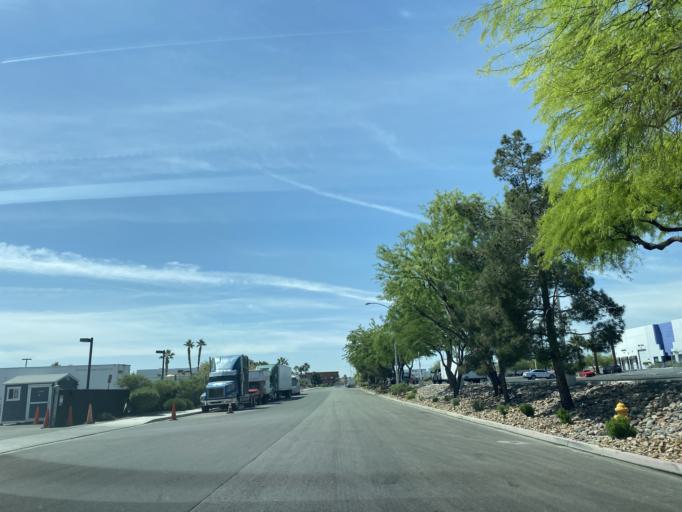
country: US
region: Nevada
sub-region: Clark County
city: Paradise
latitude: 36.0744
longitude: -115.1769
